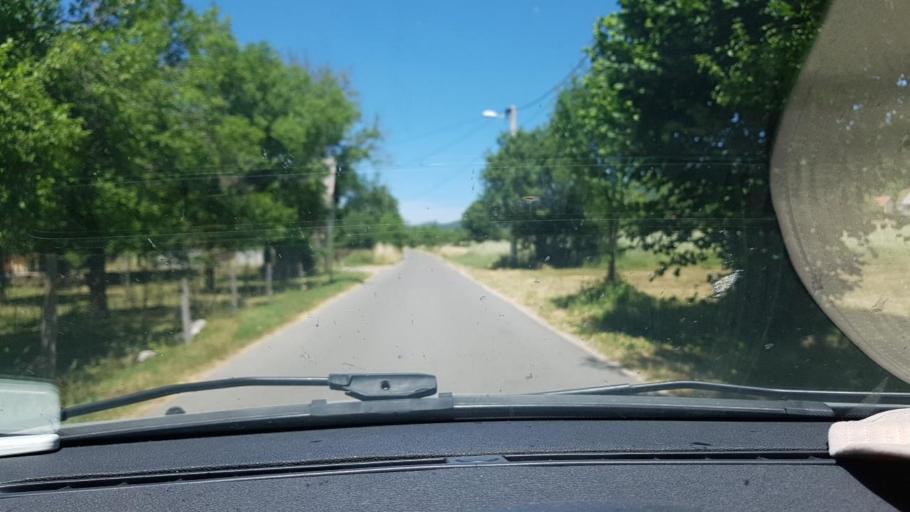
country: HR
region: Licko-Senjska
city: Otocac
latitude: 44.7917
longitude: 15.3675
